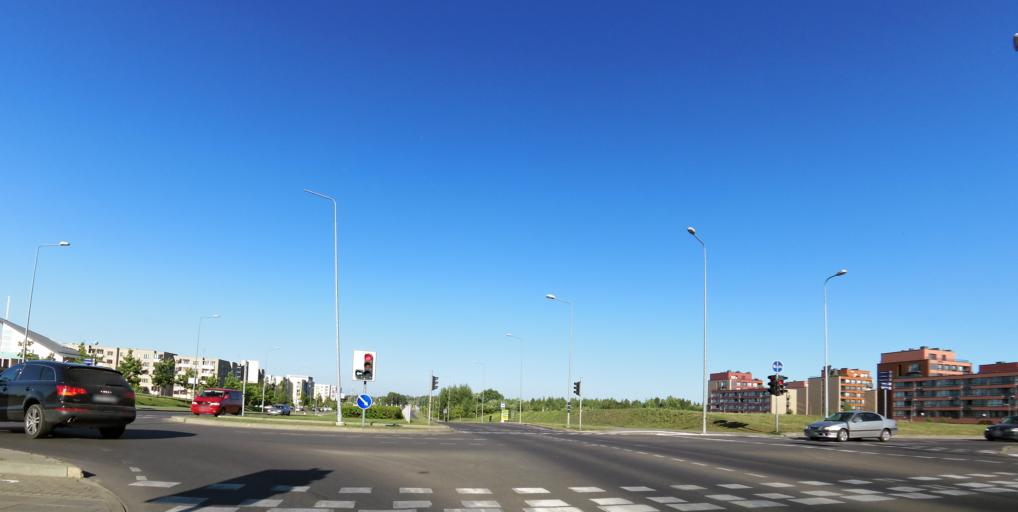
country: LT
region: Vilnius County
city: Pilaite
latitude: 54.7103
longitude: 25.1823
